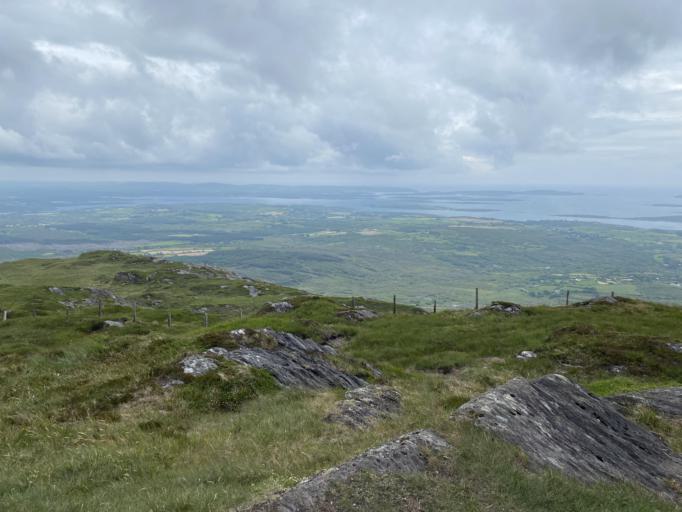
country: IE
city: Farranacoush
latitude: 51.5568
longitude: -9.5418
